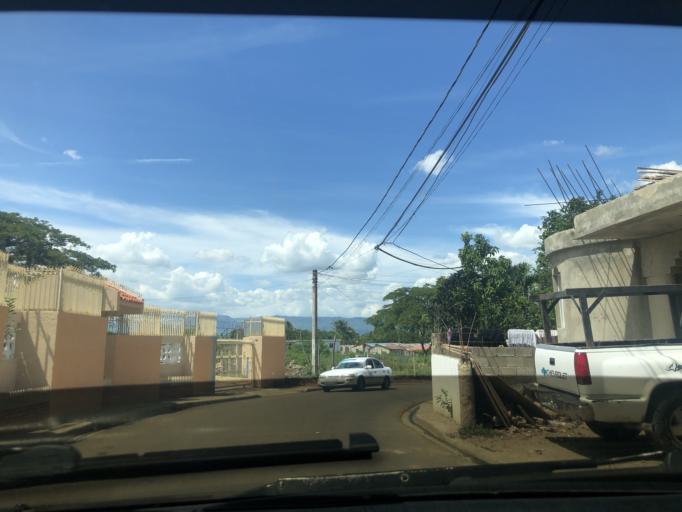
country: DO
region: Santiago
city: Santiago de los Caballeros
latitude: 19.3985
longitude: -70.6670
